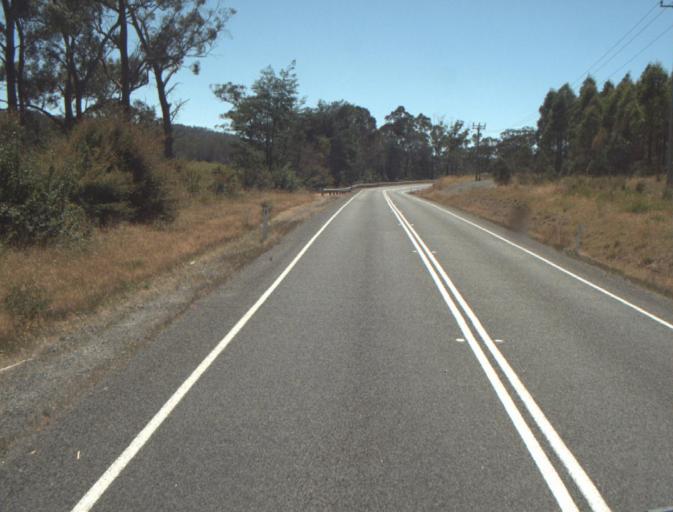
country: AU
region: Tasmania
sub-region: Launceston
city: Newstead
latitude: -41.3752
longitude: 147.3129
